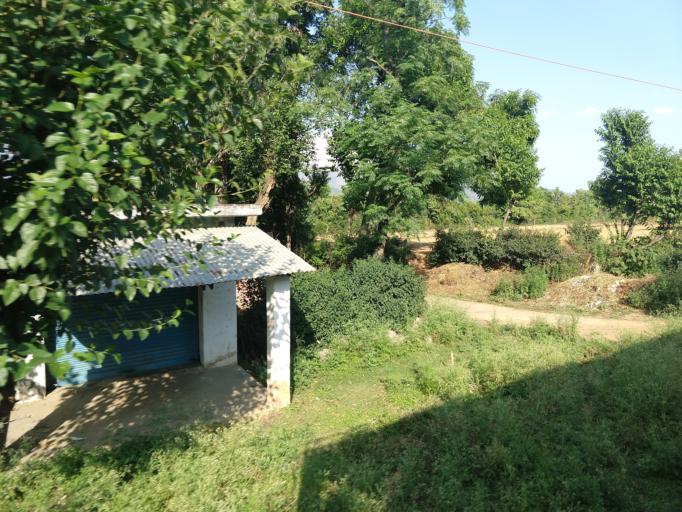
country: IN
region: Himachal Pradesh
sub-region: Chamba
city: Chowari
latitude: 32.3668
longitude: 75.9211
